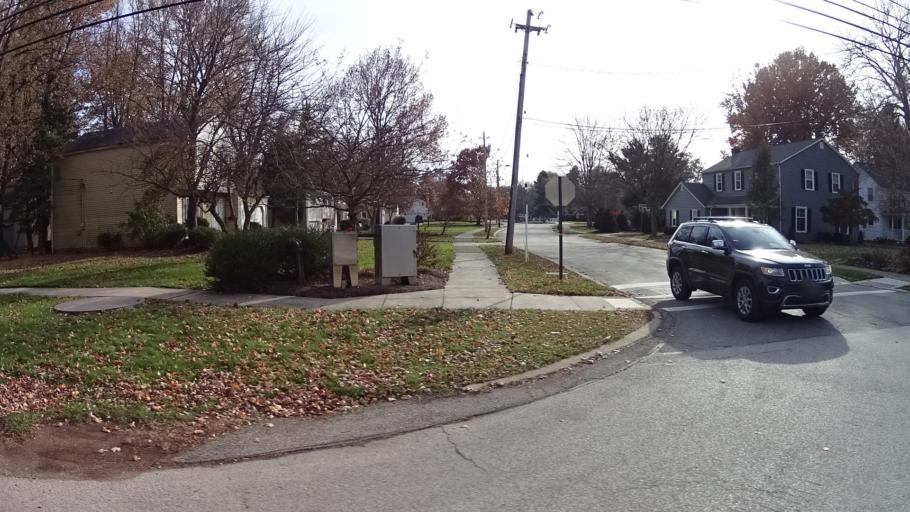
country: US
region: Ohio
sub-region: Cuyahoga County
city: Bay Village
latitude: 41.4927
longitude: -81.9643
